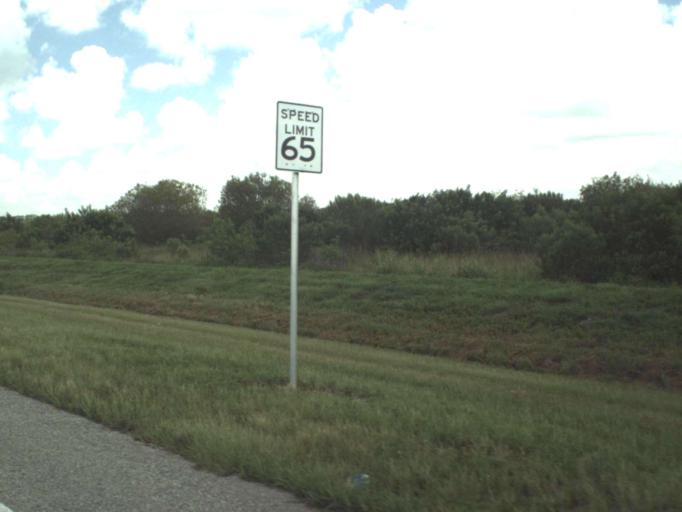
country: US
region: Florida
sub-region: Indian River County
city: West Vero Corridor
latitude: 27.6395
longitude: -80.5387
